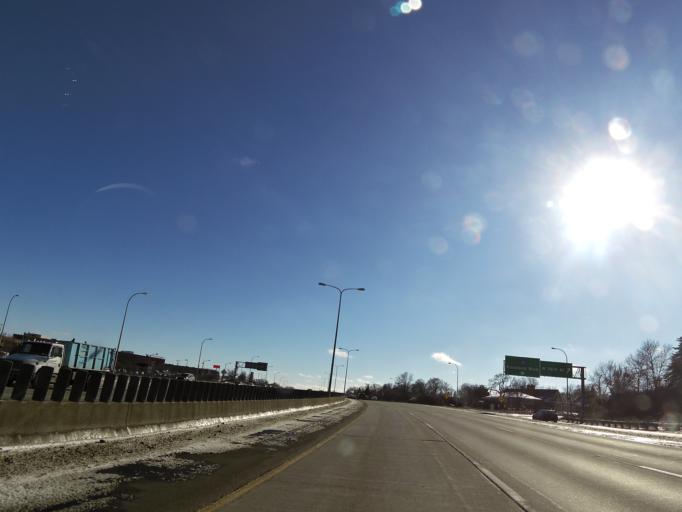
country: US
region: Minnesota
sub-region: Hennepin County
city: Saint Louis Park
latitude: 44.9367
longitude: -93.3500
